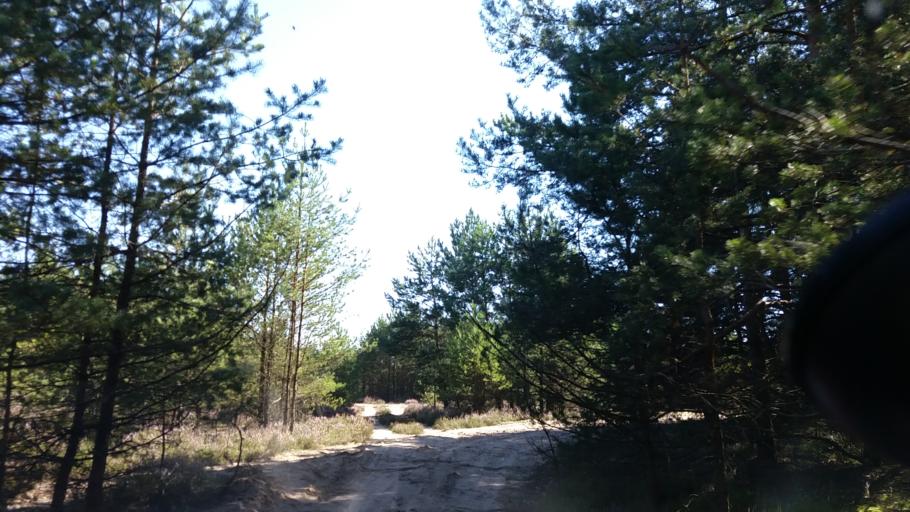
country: PL
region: West Pomeranian Voivodeship
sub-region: Powiat szczecinecki
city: Borne Sulinowo
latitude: 53.5820
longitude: 16.4971
